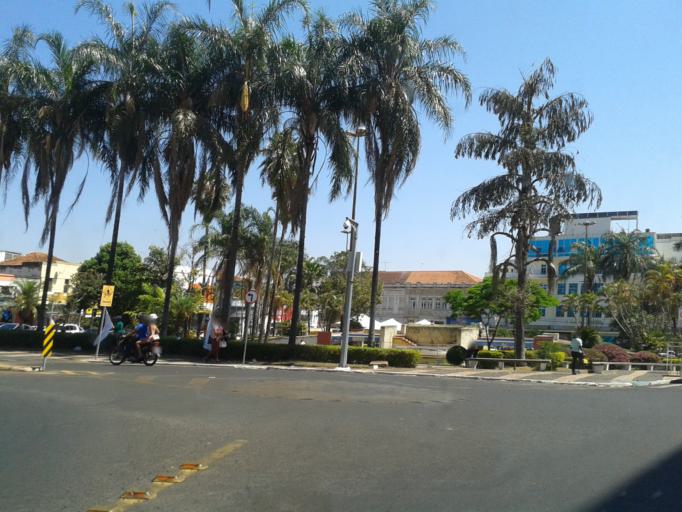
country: BR
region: Minas Gerais
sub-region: Araguari
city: Araguari
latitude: -18.6494
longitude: -48.1900
